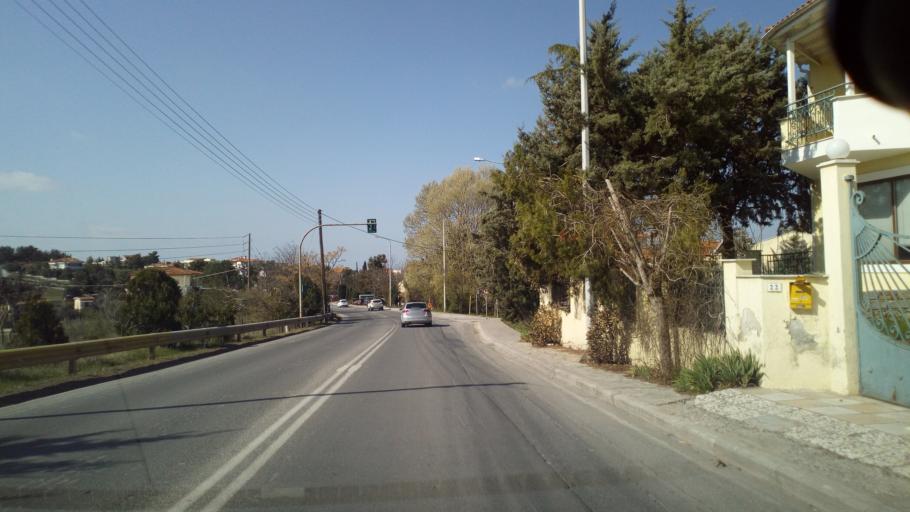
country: GR
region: Central Macedonia
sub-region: Nomos Thessalonikis
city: Panorama
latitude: 40.5816
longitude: 23.0311
